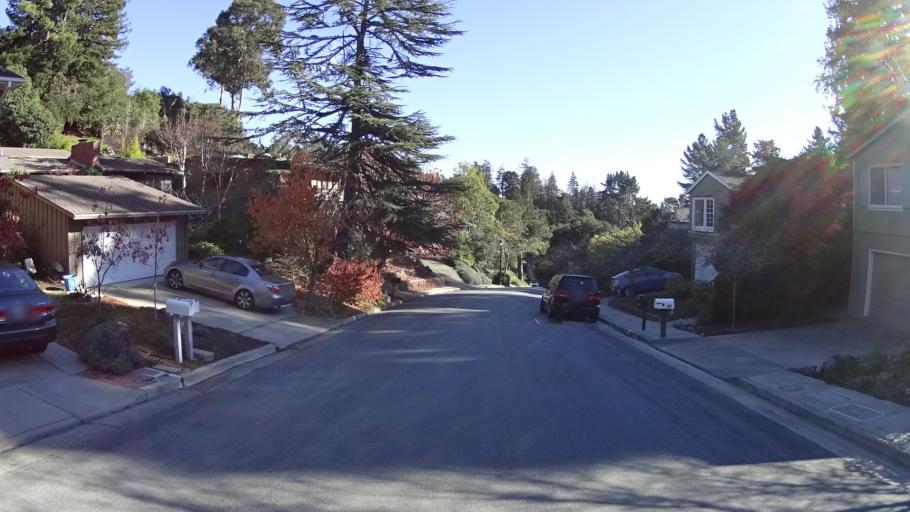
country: US
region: California
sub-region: Alameda County
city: Piedmont
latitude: 37.8267
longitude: -122.2224
